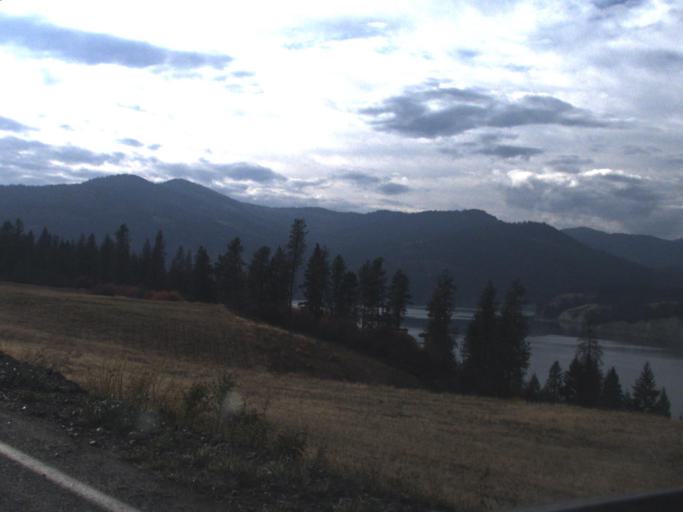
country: US
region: Washington
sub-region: Lincoln County
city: Davenport
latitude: 48.1349
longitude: -118.2016
